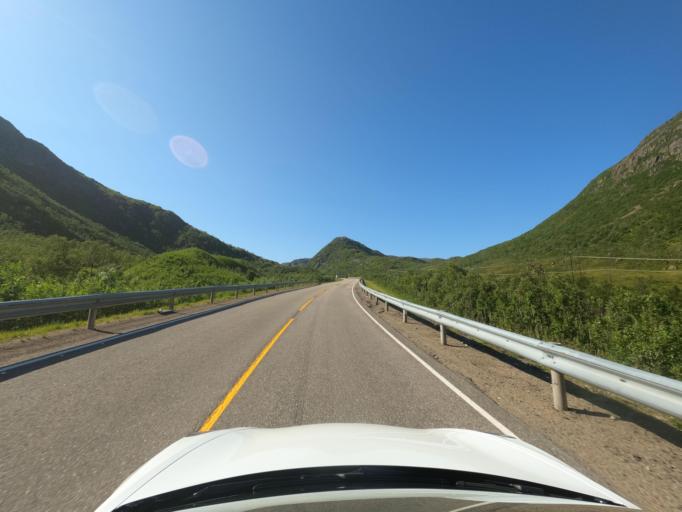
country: NO
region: Nordland
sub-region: Lodingen
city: Lodingen
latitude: 68.4920
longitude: 15.6981
